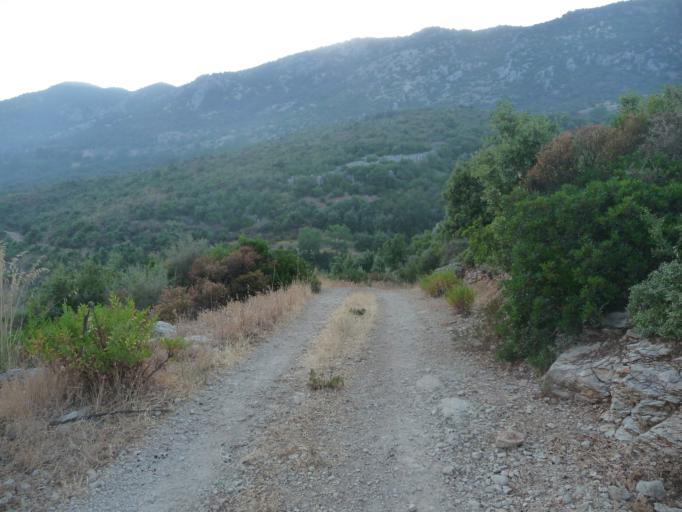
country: IT
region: Calabria
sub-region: Provincia di Reggio Calabria
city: Pazzano
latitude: 38.4547
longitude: 16.4395
